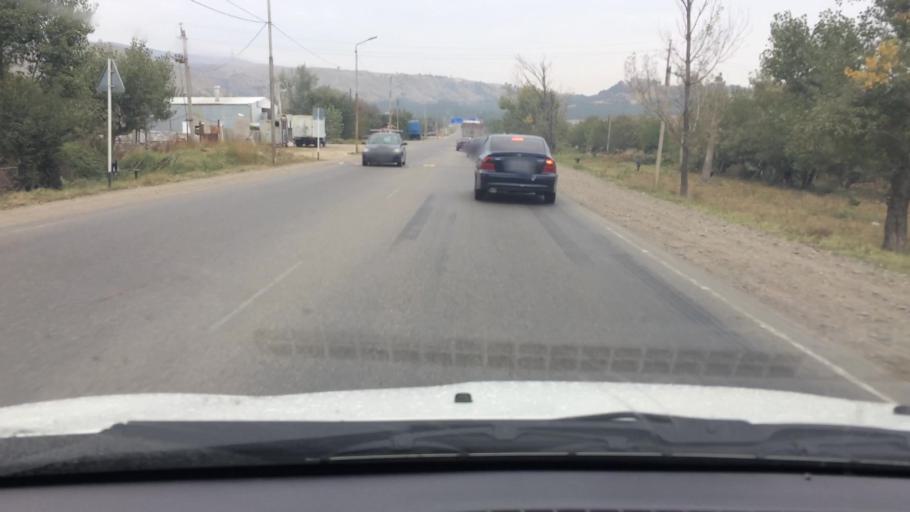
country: GE
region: T'bilisi
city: Tbilisi
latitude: 41.6114
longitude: 44.7874
